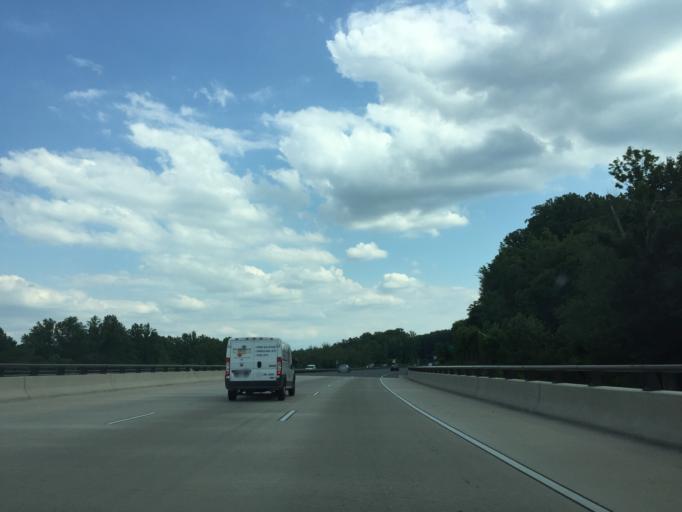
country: US
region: Maryland
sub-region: Montgomery County
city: Layhill
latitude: 39.0936
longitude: -77.0296
